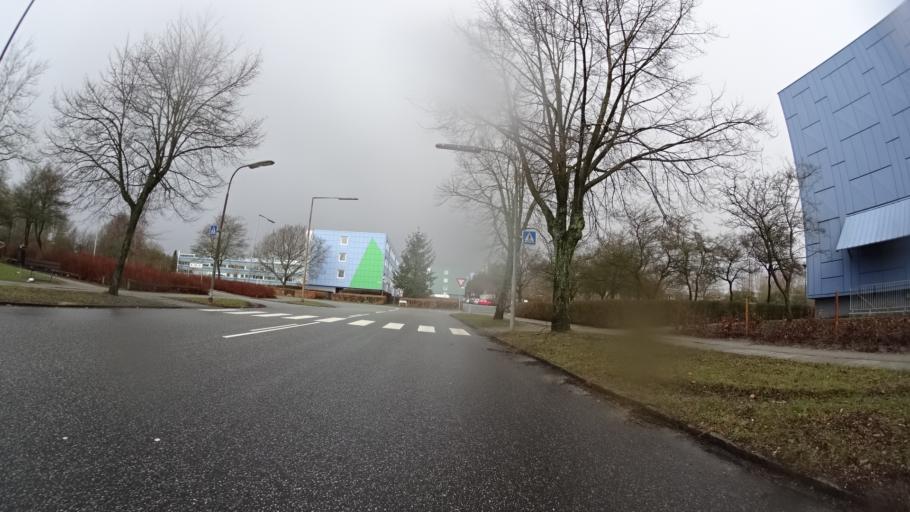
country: DK
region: Central Jutland
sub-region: Arhus Kommune
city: Arhus
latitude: 56.1666
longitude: 10.1747
